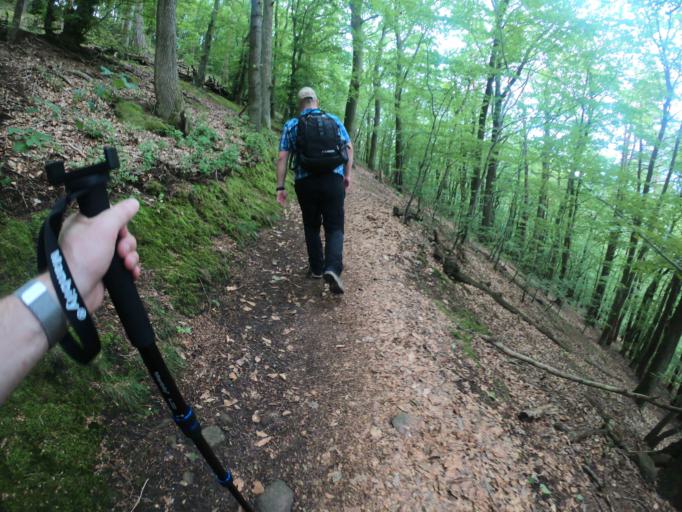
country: DE
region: Rheinland-Pfalz
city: Annweiler am Trifels
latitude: 49.1896
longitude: 7.9851
